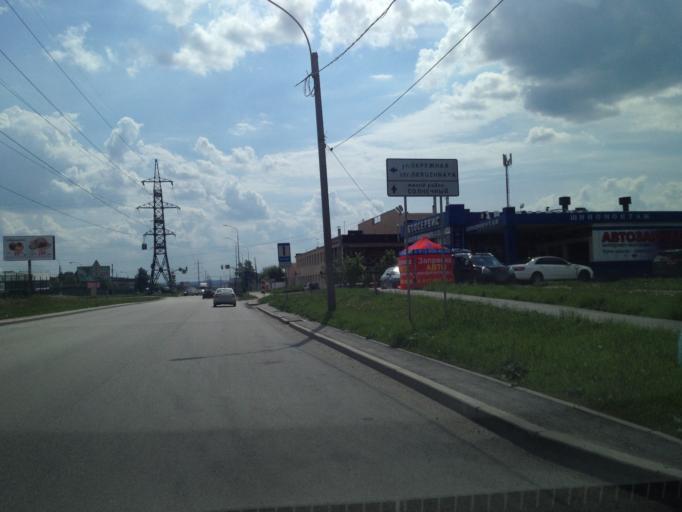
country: RU
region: Sverdlovsk
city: Sovkhoznyy
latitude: 56.7585
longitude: 60.5880
